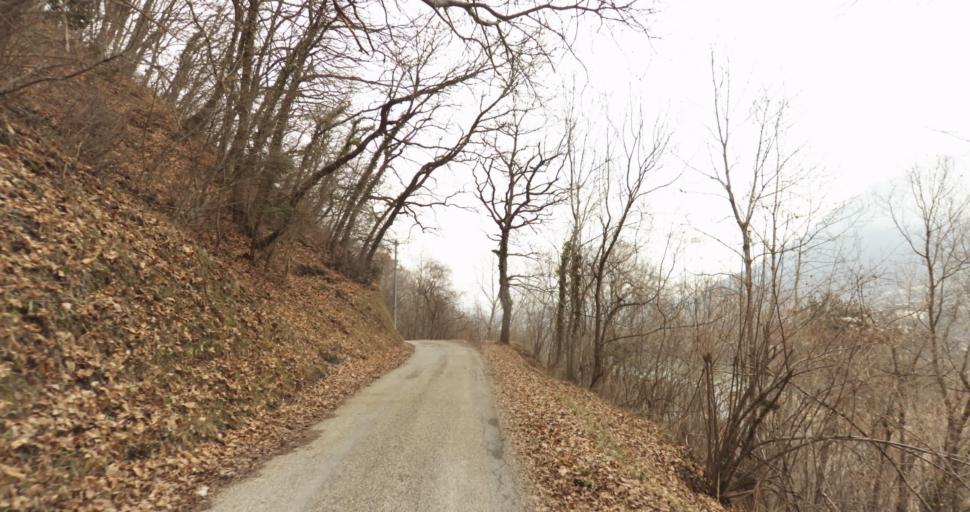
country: FR
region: Rhone-Alpes
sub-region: Departement de l'Isere
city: Saint-Georges-de-Commiers
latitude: 45.0366
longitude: 5.6910
